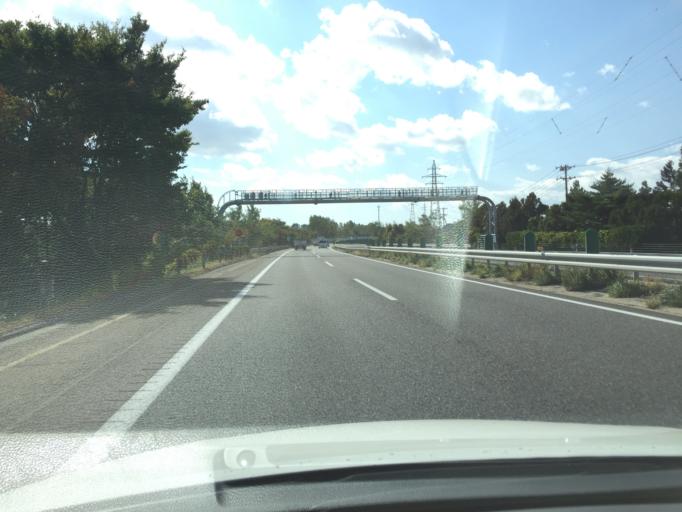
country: JP
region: Fukushima
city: Koriyama
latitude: 37.4198
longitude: 140.3327
